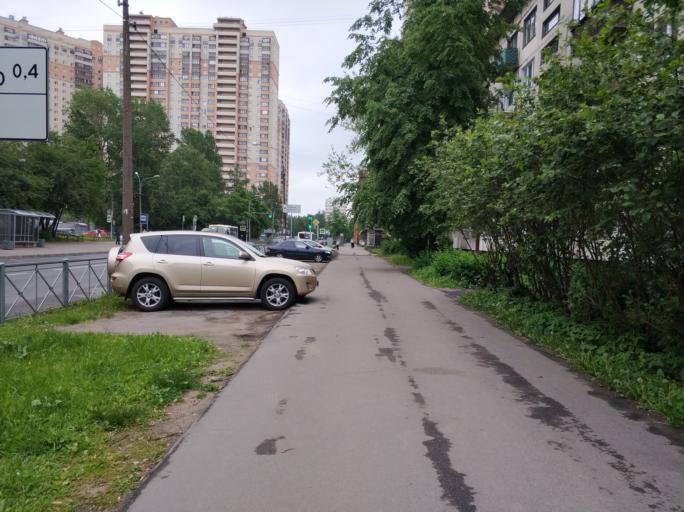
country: RU
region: St.-Petersburg
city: Grazhdanka
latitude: 60.0328
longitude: 30.3997
